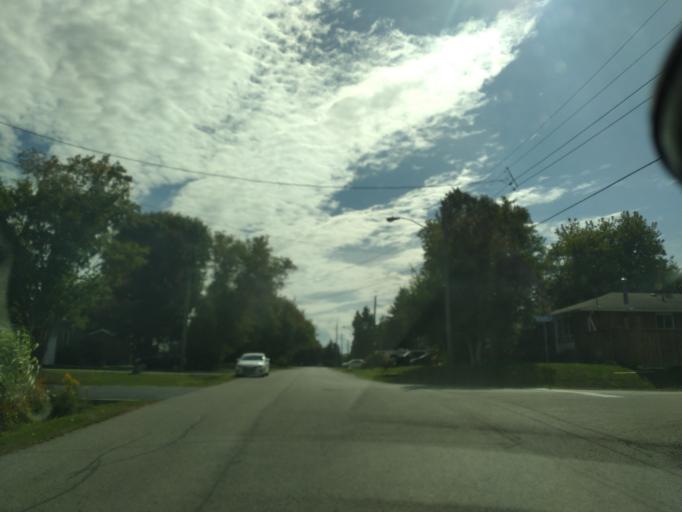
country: CA
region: Ontario
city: Newmarket
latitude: 44.0979
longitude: -79.4843
